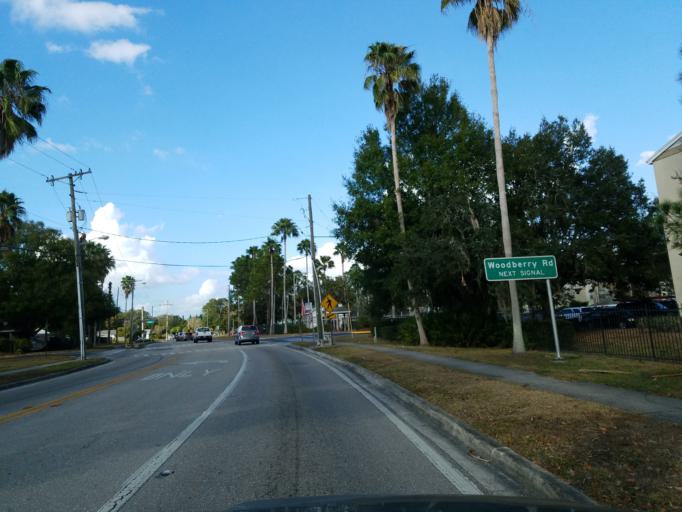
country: US
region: Florida
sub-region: Hillsborough County
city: Mango
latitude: 27.9508
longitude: -82.3253
